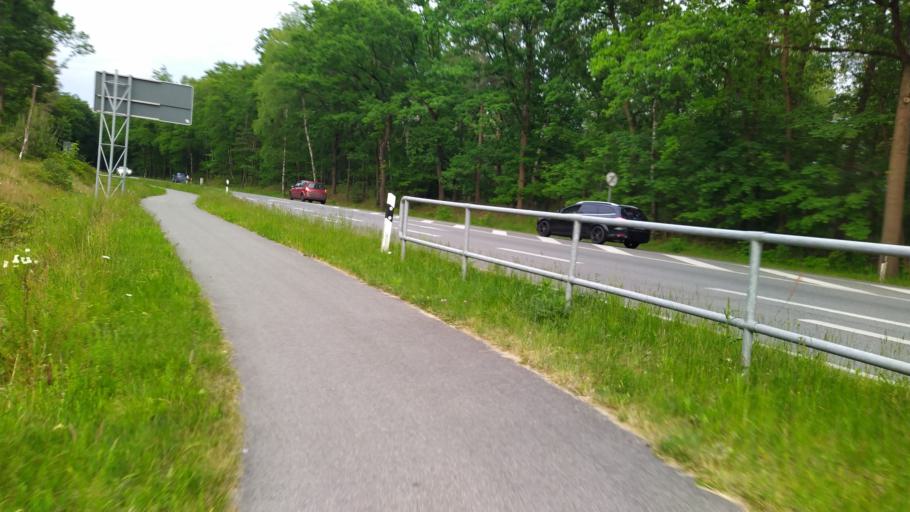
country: DE
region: Lower Saxony
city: Neu Wulmstorf
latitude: 53.4553
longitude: 9.7729
